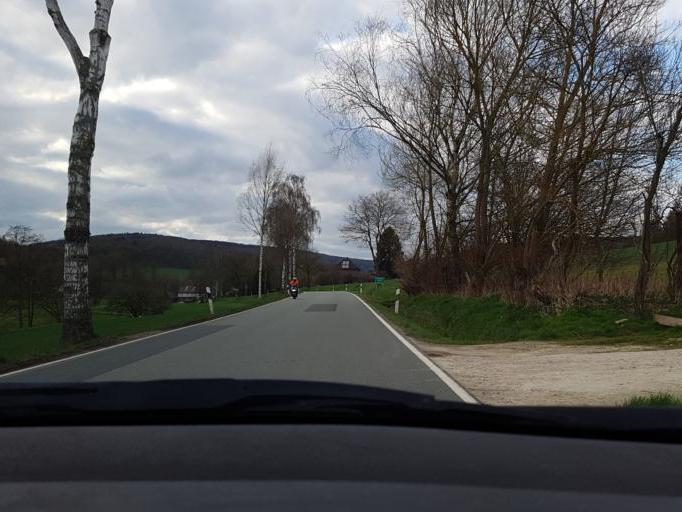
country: DE
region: Lower Saxony
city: Bodenfelde
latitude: 51.6787
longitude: 9.5312
